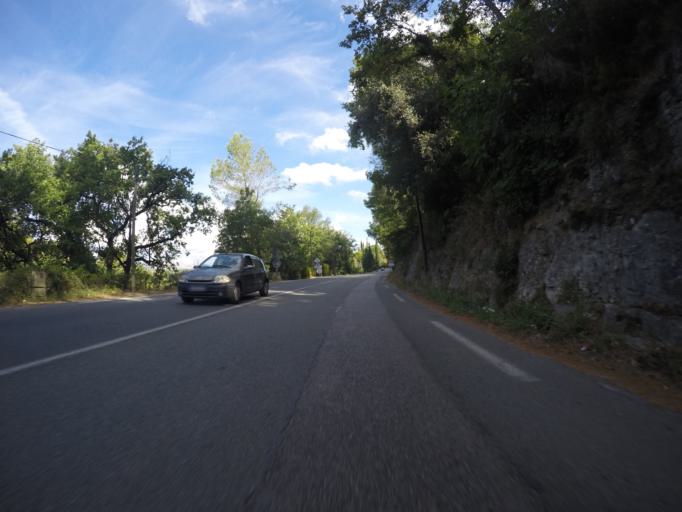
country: FR
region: Provence-Alpes-Cote d'Azur
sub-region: Departement des Alpes-Maritimes
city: Le Rouret
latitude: 43.6730
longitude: 7.0240
